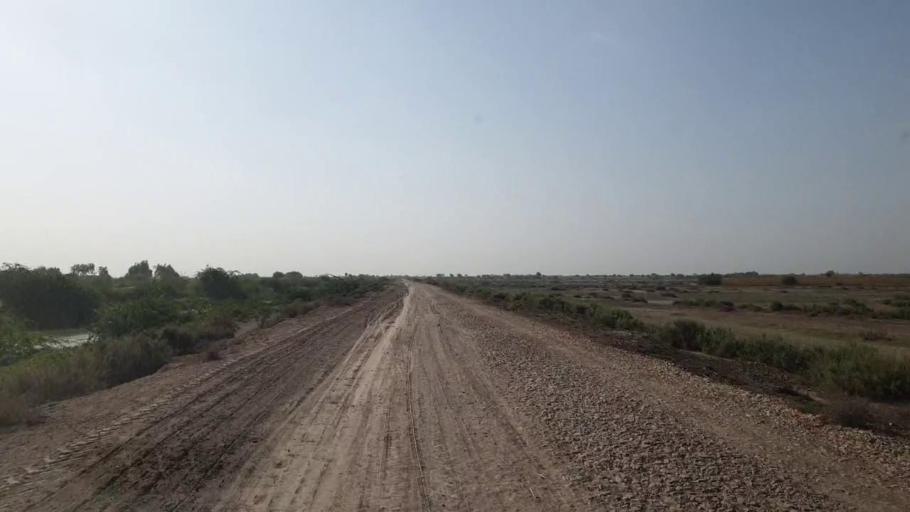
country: PK
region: Sindh
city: Kadhan
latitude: 24.6351
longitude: 69.0725
